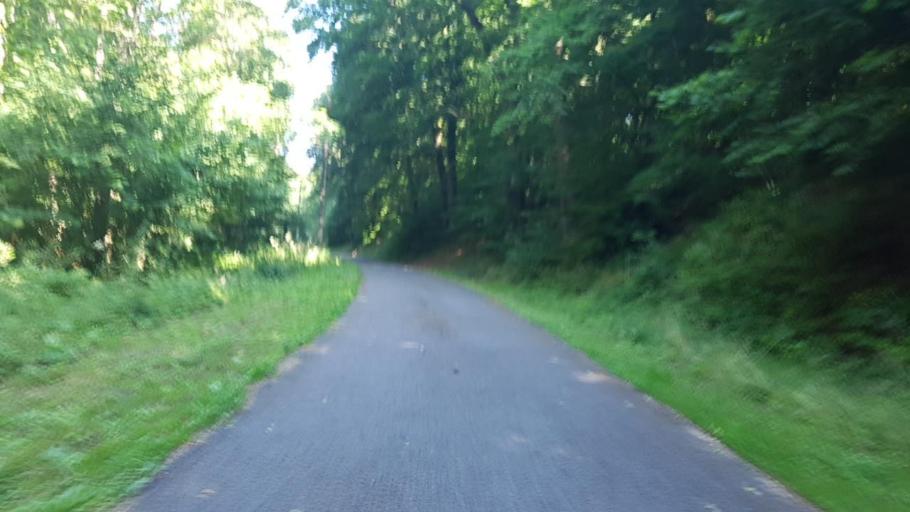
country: FR
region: Nord-Pas-de-Calais
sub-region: Departement du Nord
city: Anor
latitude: 49.9541
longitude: 4.1057
